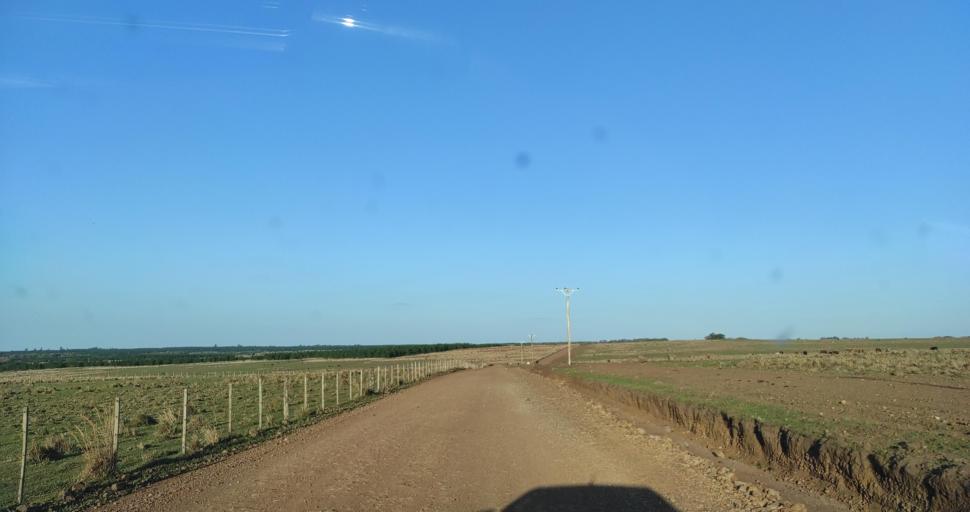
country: PY
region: Itapua
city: Carmen del Parana
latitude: -27.4120
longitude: -56.1449
